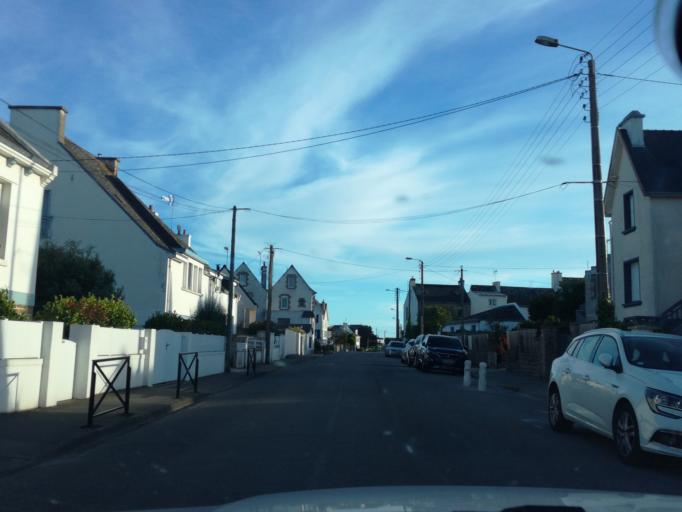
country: FR
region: Brittany
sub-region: Departement du Morbihan
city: Quiberon
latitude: 47.4812
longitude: -3.1252
